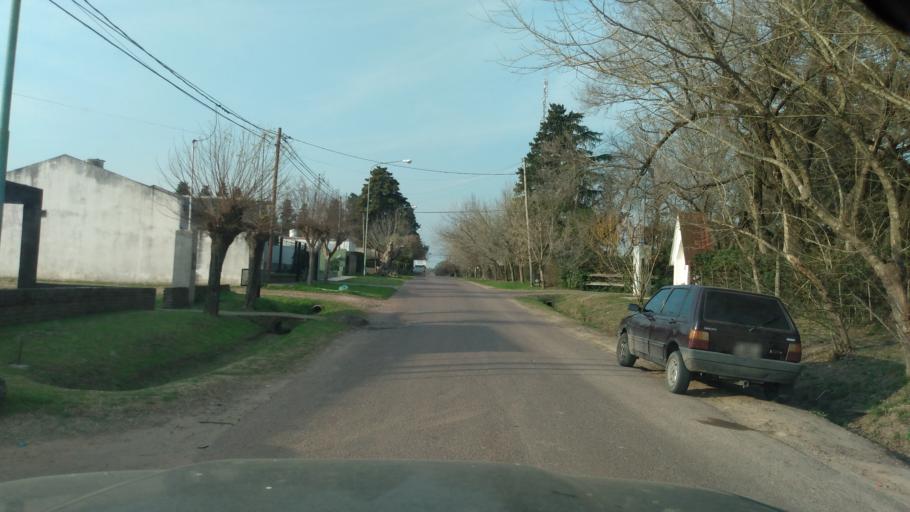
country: AR
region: Buenos Aires
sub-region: Partido de Lujan
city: Lujan
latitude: -34.5770
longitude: -59.1793
